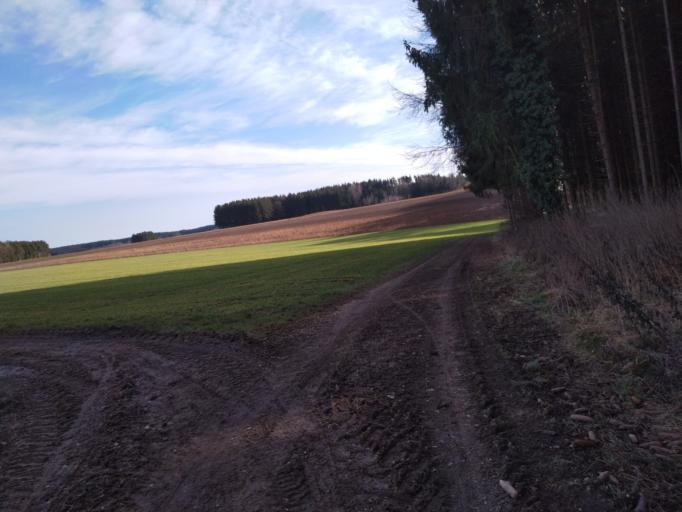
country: DE
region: Bavaria
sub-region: Swabia
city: Rettenbach
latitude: 48.4320
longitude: 10.3217
